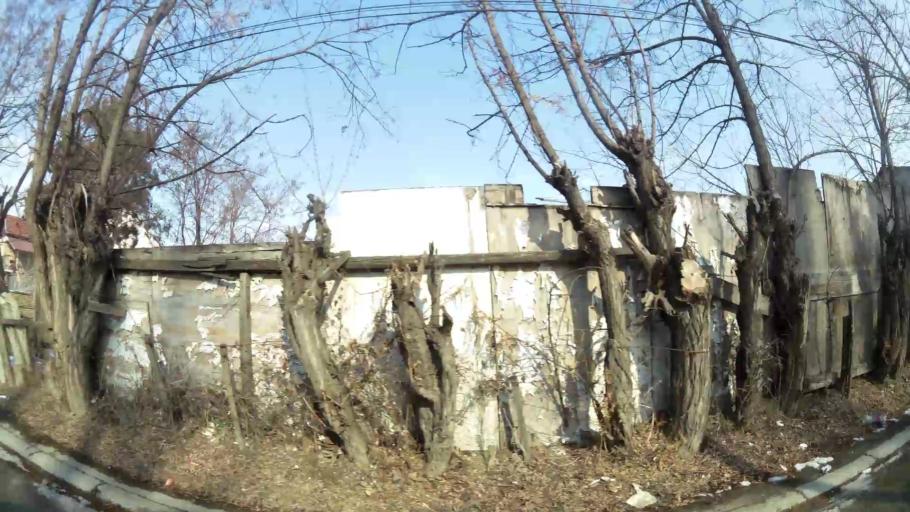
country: MK
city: Krushopek
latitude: 42.0156
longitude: 21.3784
